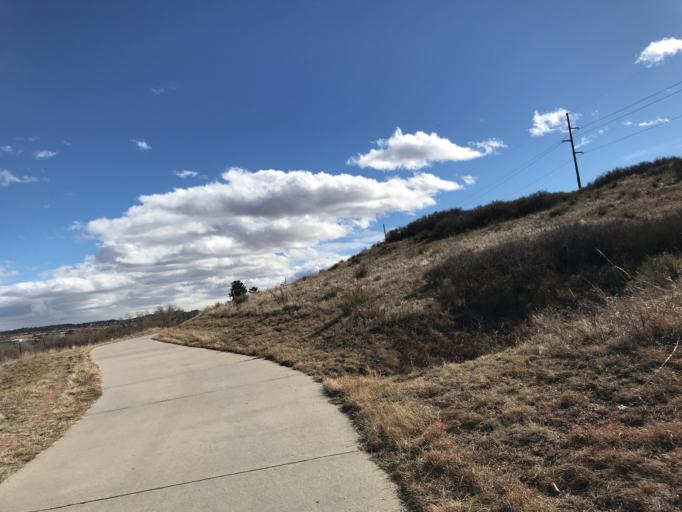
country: US
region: Colorado
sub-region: Douglas County
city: Castle Pines
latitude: 39.4112
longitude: -104.8848
